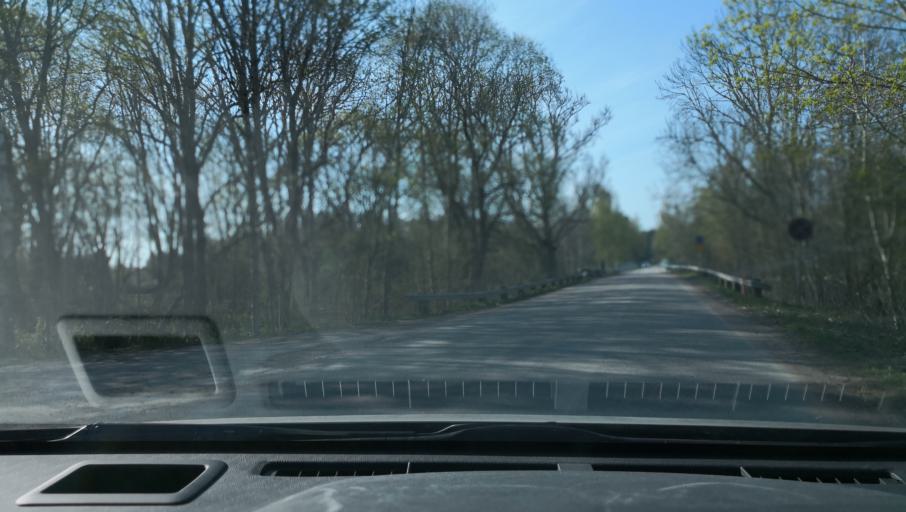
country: SE
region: Uppsala
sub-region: Heby Kommun
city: Tarnsjo
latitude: 60.2667
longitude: 16.9161
